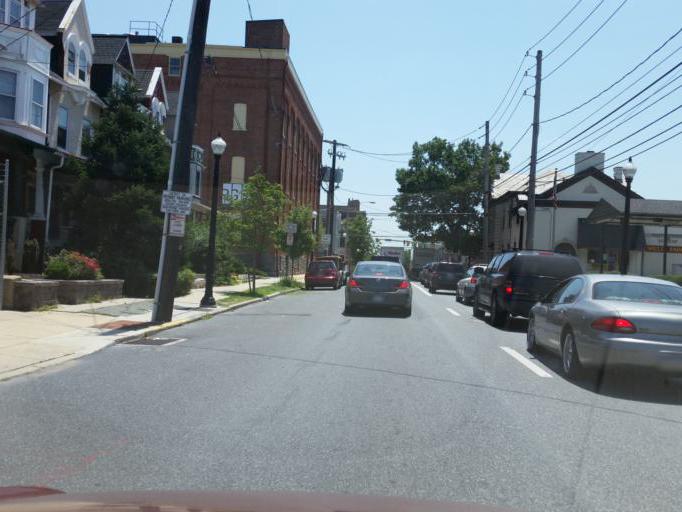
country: US
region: Pennsylvania
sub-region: Lancaster County
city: Lancaster
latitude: 40.0465
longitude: -76.3093
